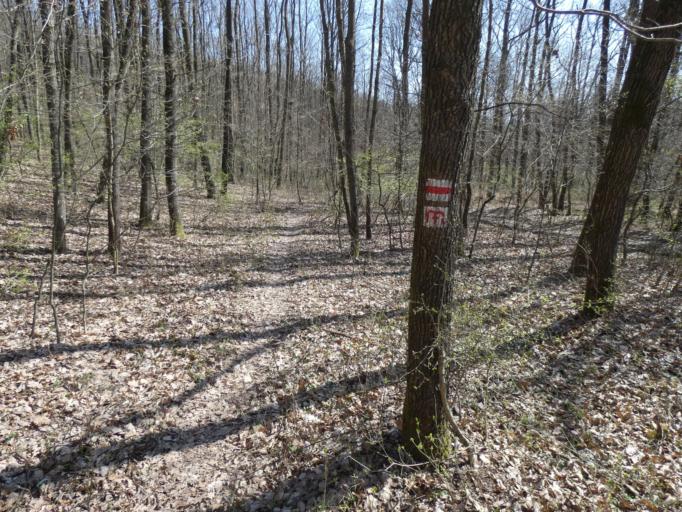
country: HU
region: Pest
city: Szob
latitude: 47.8700
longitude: 18.9152
